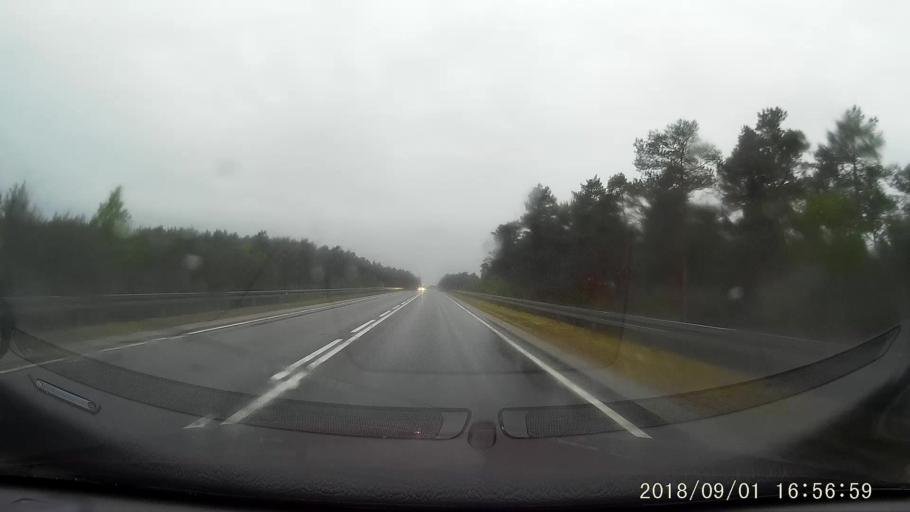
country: PL
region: Lubusz
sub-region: Powiat zielonogorski
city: Swidnica
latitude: 51.9360
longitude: 15.4284
